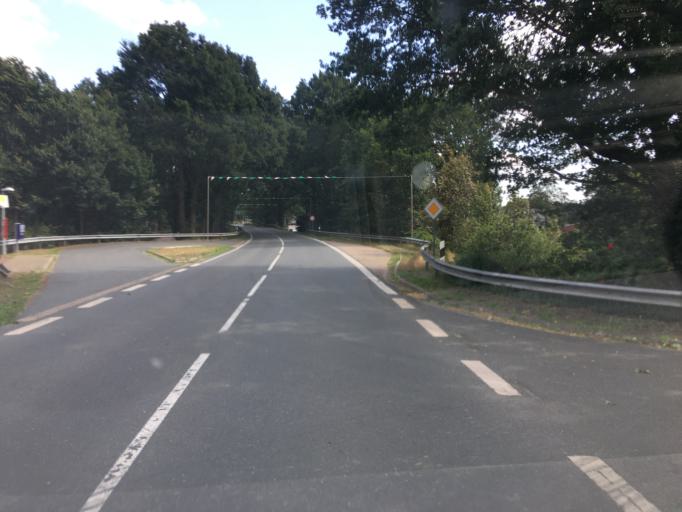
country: DE
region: Lower Saxony
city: Friesoythe
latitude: 53.0833
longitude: 7.8335
